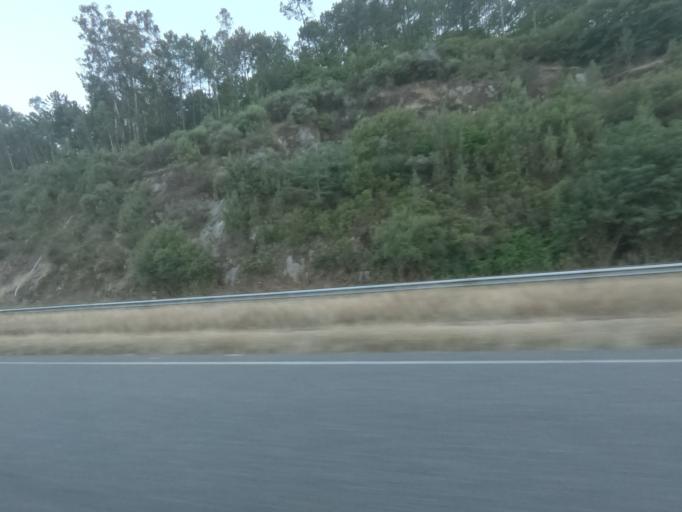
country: ES
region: Galicia
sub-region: Provincia de Pontevedra
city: Ponteareas
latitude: 42.1760
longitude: -8.5586
